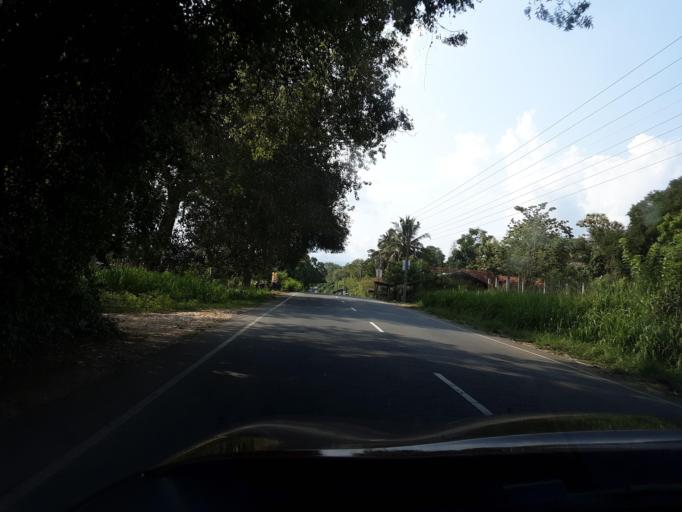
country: LK
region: Uva
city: Haputale
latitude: 6.6016
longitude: 81.1390
